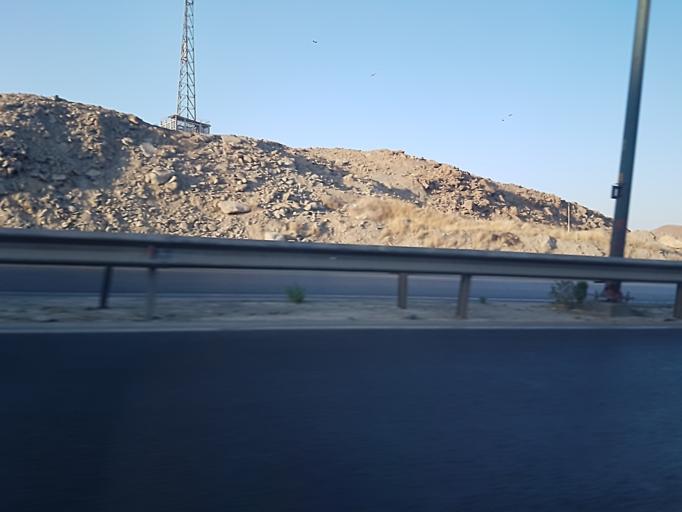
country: IR
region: Markazi
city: Arak
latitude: 34.0697
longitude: 49.7140
